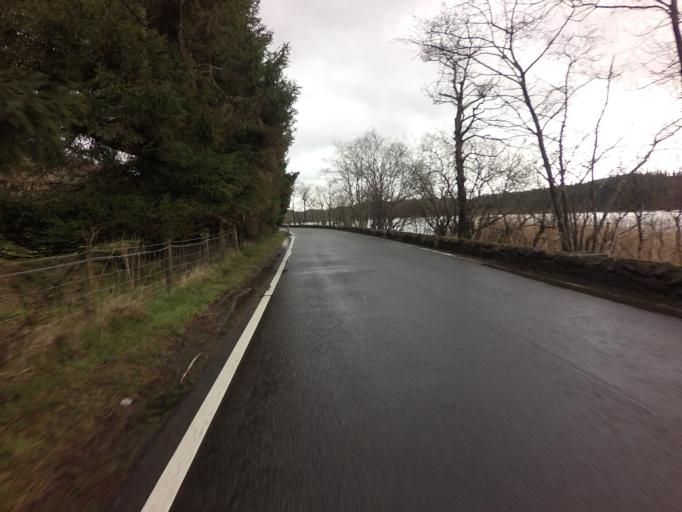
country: GB
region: Scotland
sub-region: Stirling
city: Killearn
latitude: 56.1875
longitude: -4.4775
